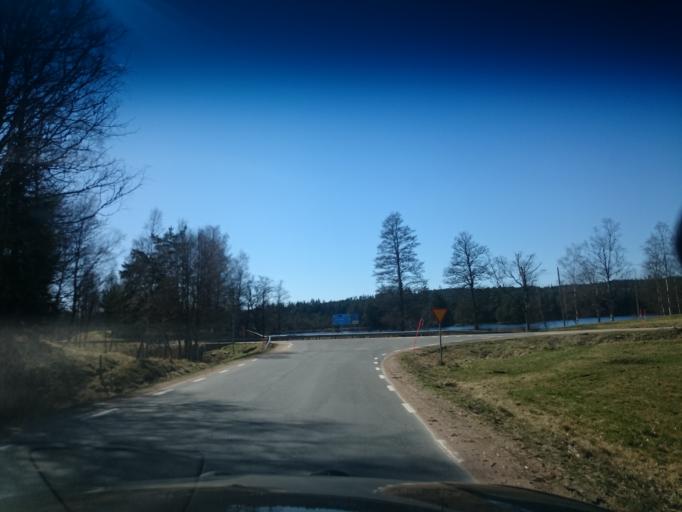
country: SE
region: Joenkoeping
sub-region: Vetlanda Kommun
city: Landsbro
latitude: 57.2192
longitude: 14.9533
